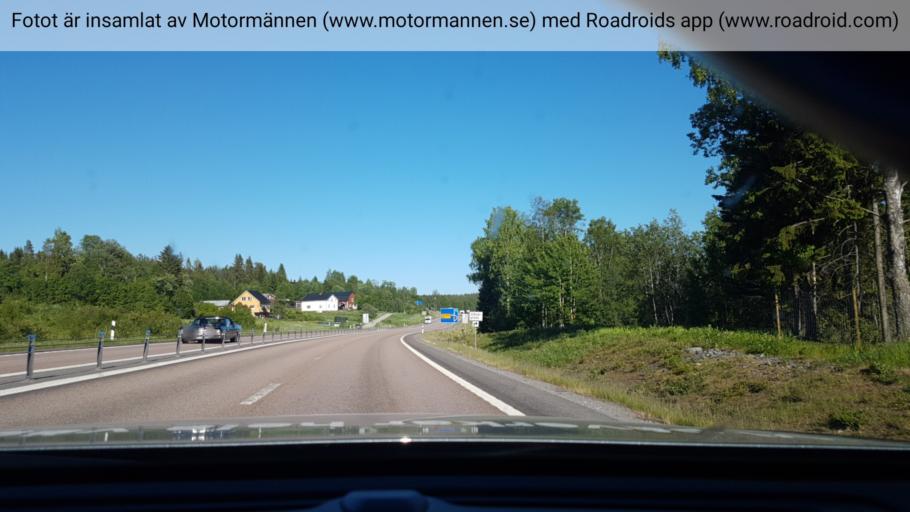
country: SE
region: Vaesternorrland
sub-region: Timra Kommun
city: Soraker
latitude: 62.5582
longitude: 17.6535
